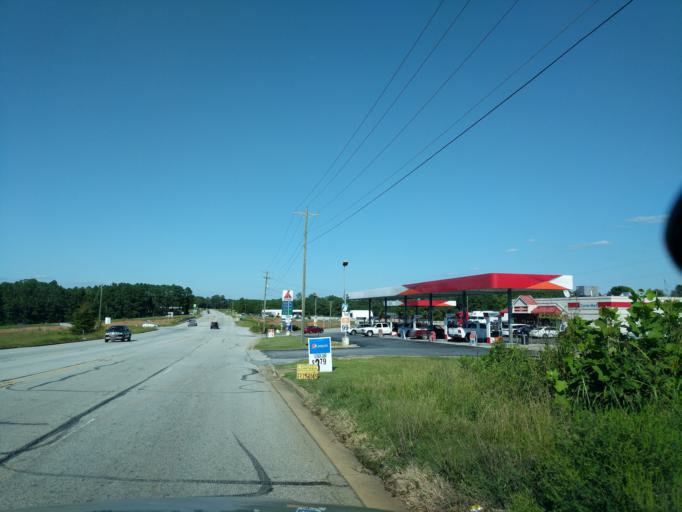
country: US
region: South Carolina
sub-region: Laurens County
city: Clinton
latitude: 34.4952
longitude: -81.8464
